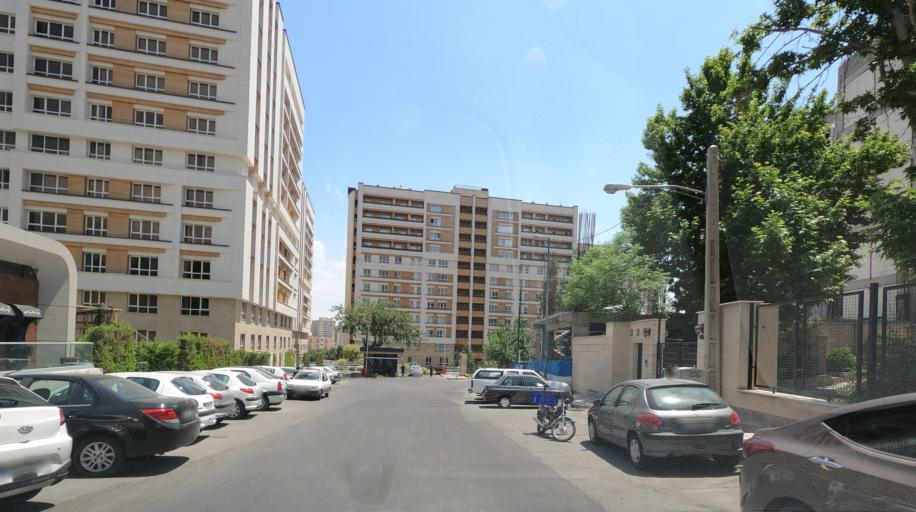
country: IR
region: Tehran
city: Tajrish
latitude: 35.7897
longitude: 51.3854
